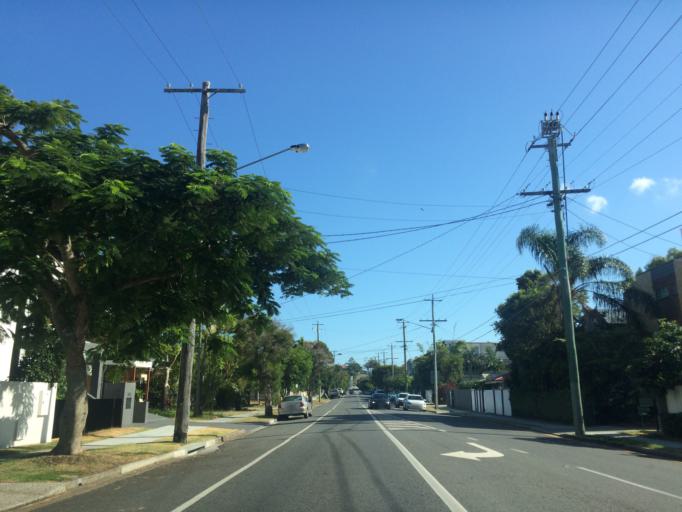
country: AU
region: Queensland
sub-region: Brisbane
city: Balmoral
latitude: -27.4564
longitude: 153.0614
